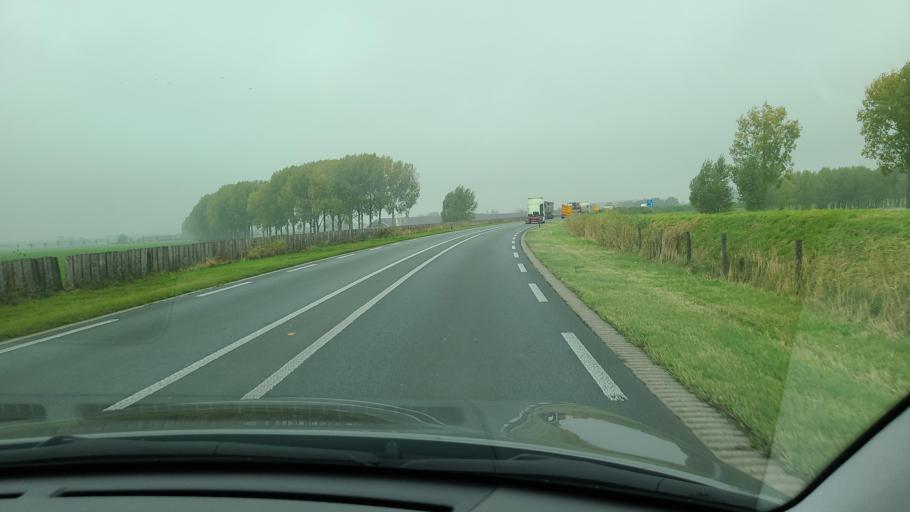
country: NL
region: Gelderland
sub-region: Gemeente Tiel
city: Tiel
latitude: 51.8707
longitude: 5.5006
